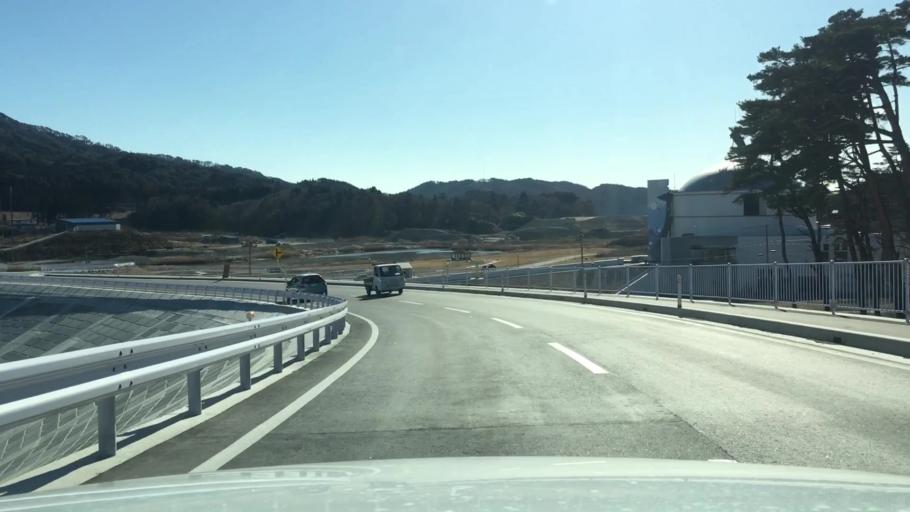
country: JP
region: Iwate
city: Yamada
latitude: 39.4382
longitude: 141.9754
